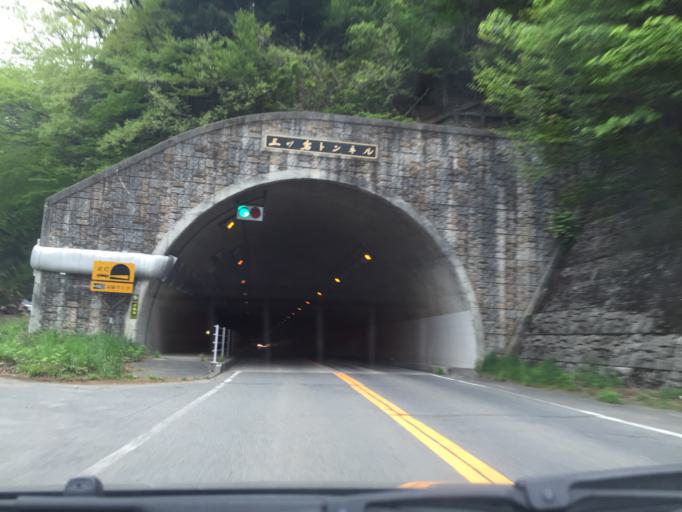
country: JP
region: Tochigi
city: Nikko
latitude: 36.8732
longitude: 139.7051
